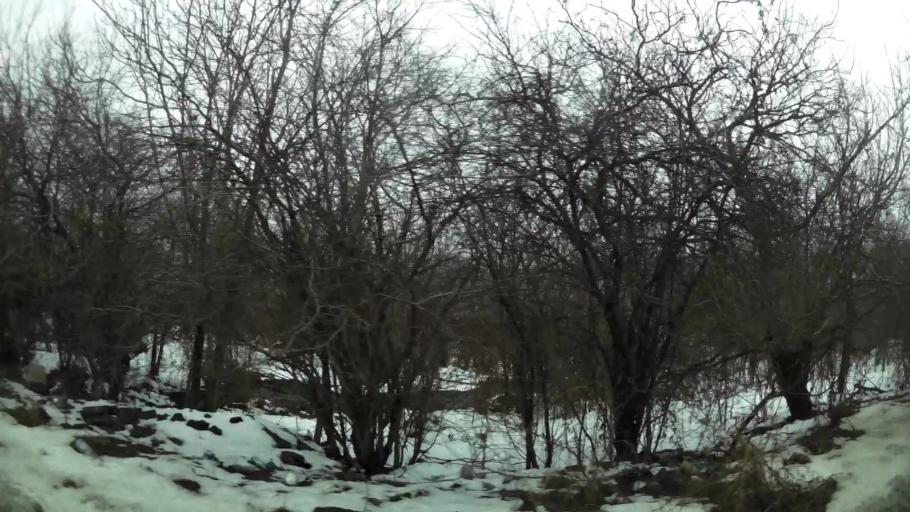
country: RS
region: Central Serbia
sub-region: Belgrade
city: Zvezdara
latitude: 44.7656
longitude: 20.5211
